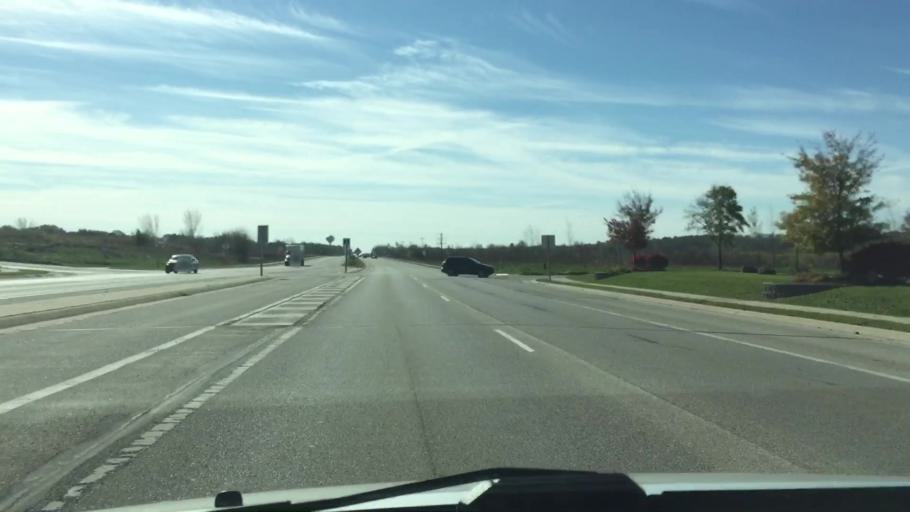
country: US
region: Wisconsin
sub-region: Waukesha County
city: Sussex
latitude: 43.1352
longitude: -88.2440
